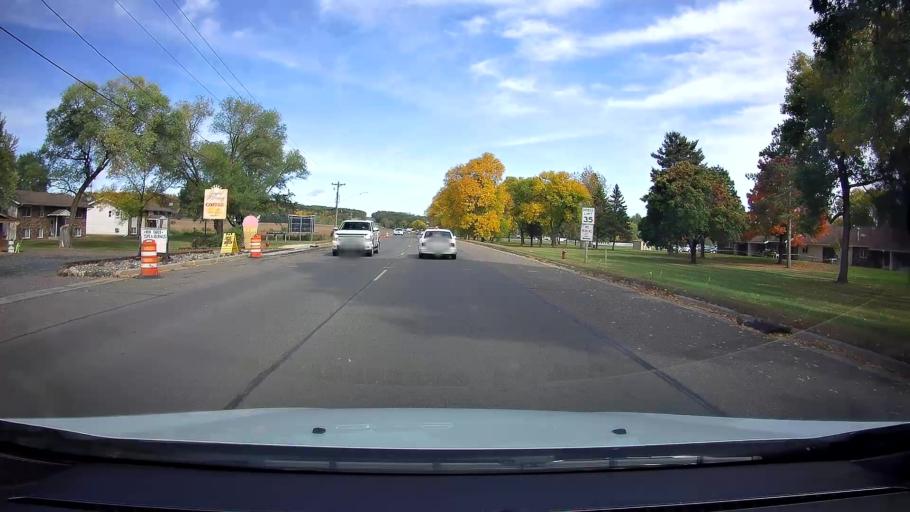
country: US
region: Wisconsin
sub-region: Polk County
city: Saint Croix Falls
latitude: 45.3577
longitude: -92.6368
